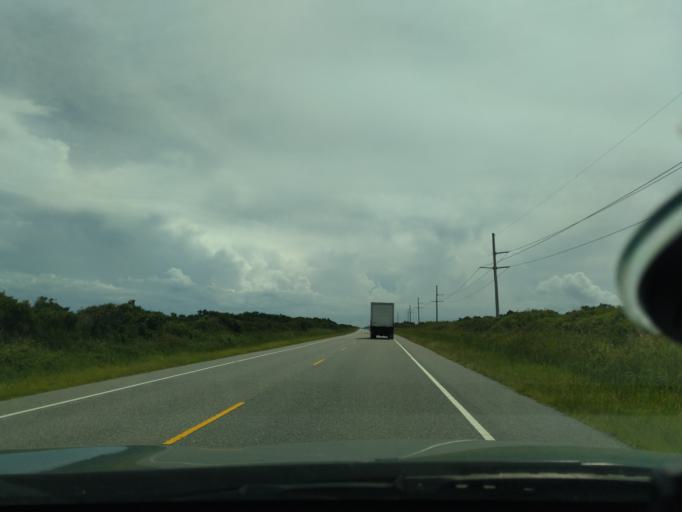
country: US
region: North Carolina
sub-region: Dare County
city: Buxton
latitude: 35.4663
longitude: -75.4839
